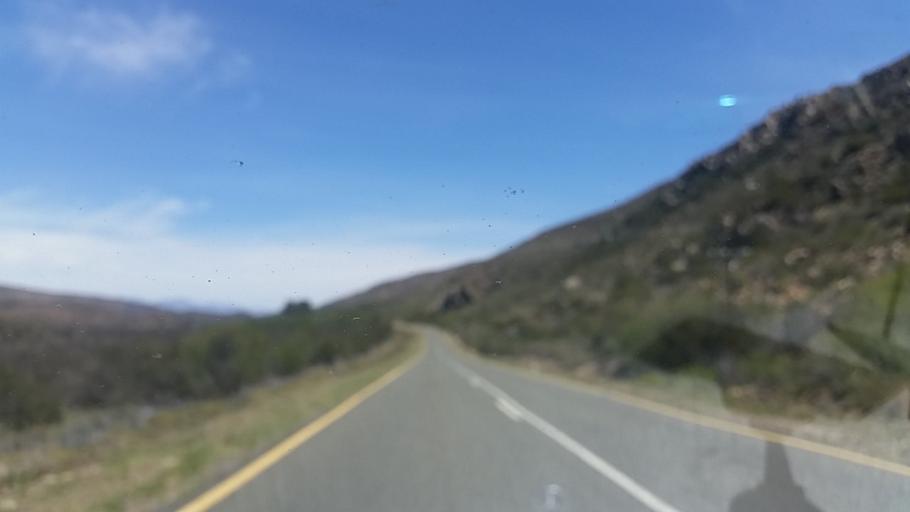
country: ZA
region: Eastern Cape
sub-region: Cacadu District Municipality
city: Willowmore
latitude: -33.3885
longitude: 23.3799
